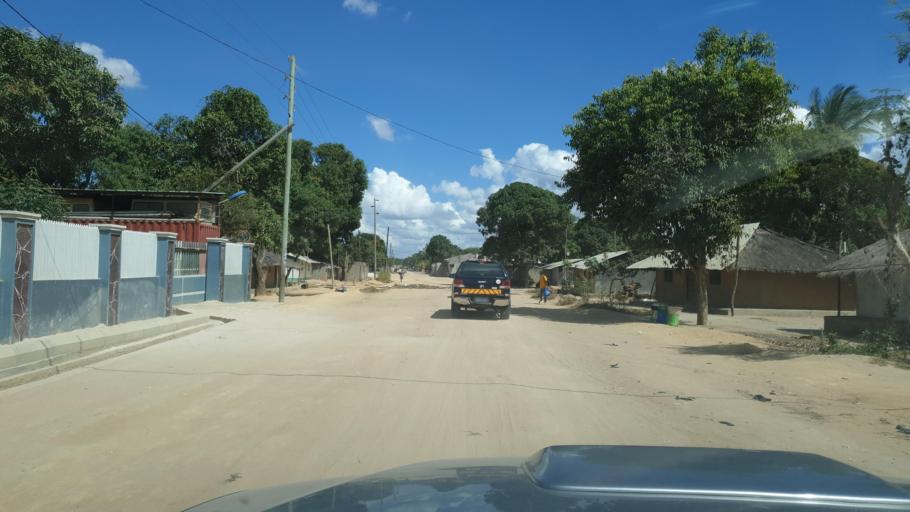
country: MZ
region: Nampula
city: Nacala
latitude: -14.5730
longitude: 40.6919
